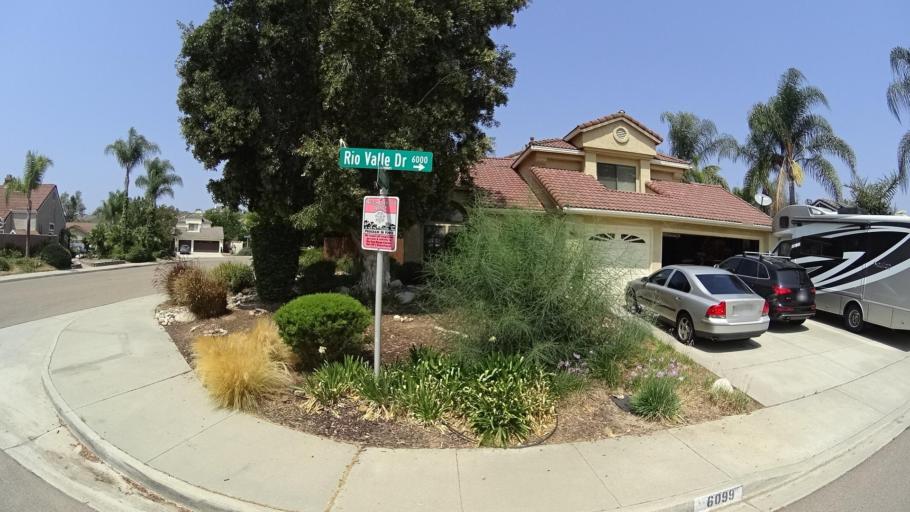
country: US
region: California
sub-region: San Diego County
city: Bonsall
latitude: 33.2923
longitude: -117.2266
